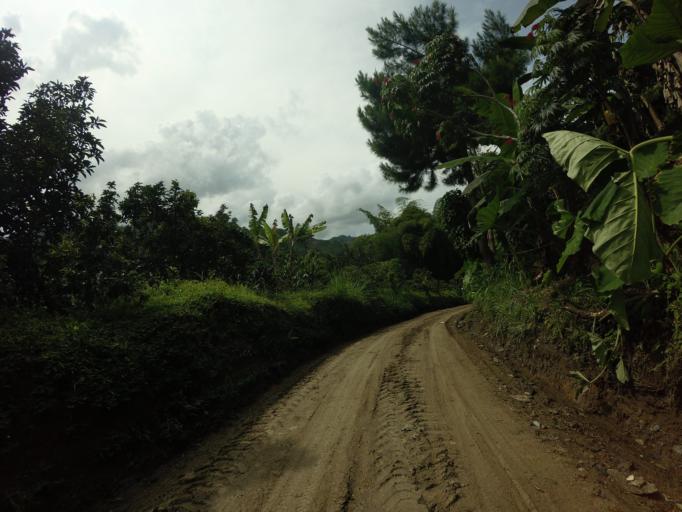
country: CO
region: Caldas
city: Marquetalia
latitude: 5.3255
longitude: -75.0457
